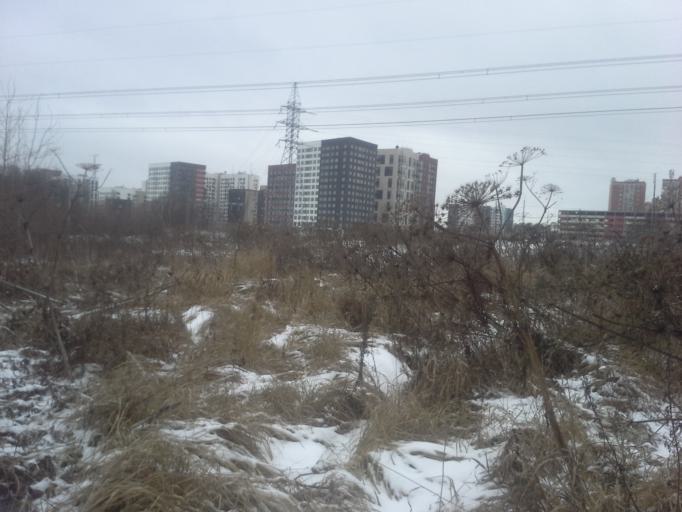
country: RU
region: Moskovskaya
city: Kommunarka
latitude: 55.5727
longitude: 37.4984
